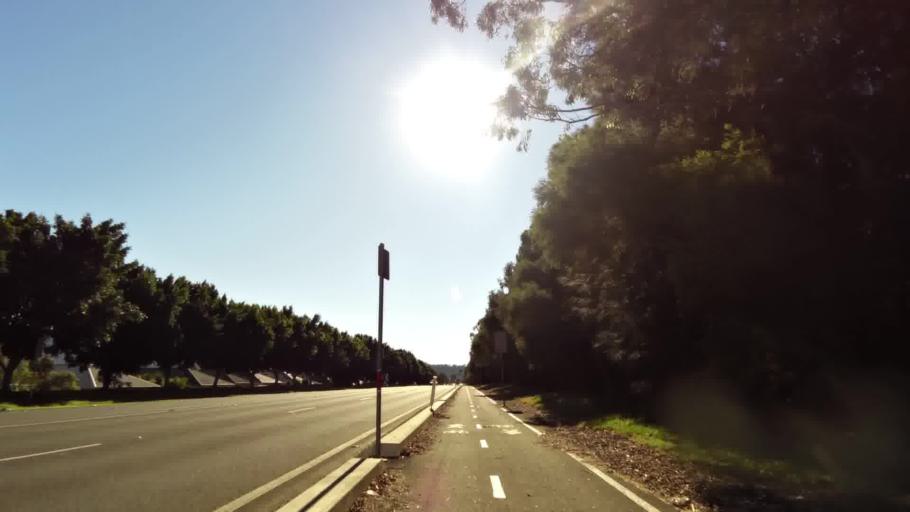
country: AU
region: New South Wales
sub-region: Wollongong
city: Koonawarra
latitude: -34.4881
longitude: 150.7982
